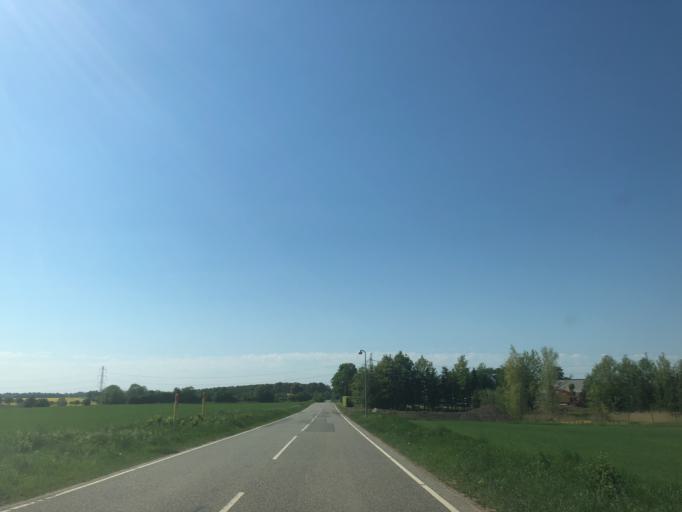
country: DK
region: Capital Region
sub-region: Hoje-Taastrup Kommune
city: Flong
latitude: 55.6280
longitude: 12.2357
